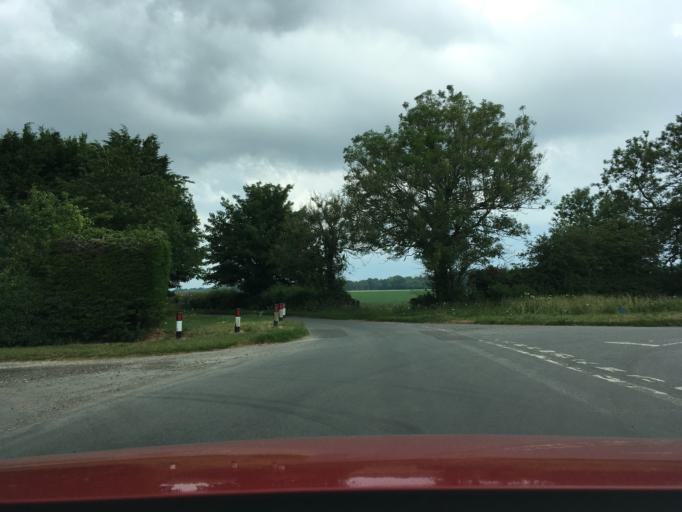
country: GB
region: England
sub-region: Gloucestershire
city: Coates
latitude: 51.7377
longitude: -2.0577
